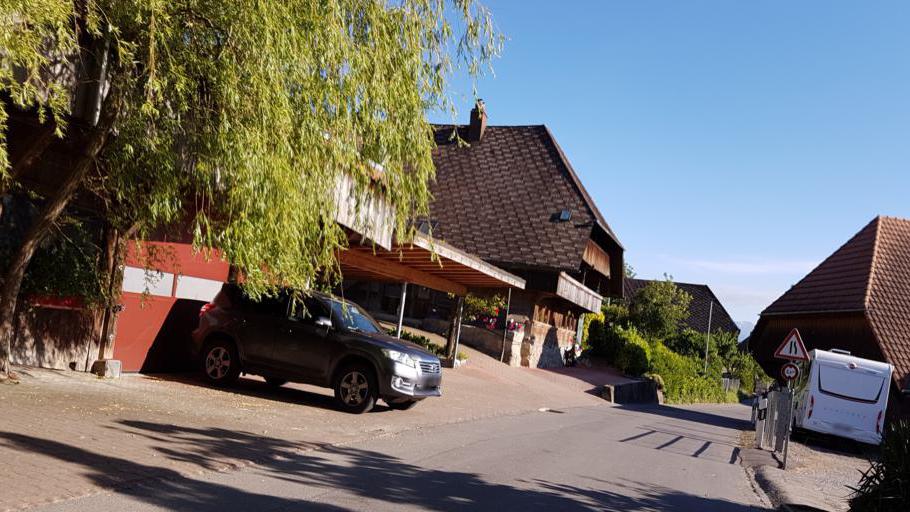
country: CH
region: Bern
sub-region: Bern-Mittelland District
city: Taegertschi
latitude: 46.9051
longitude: 7.5819
